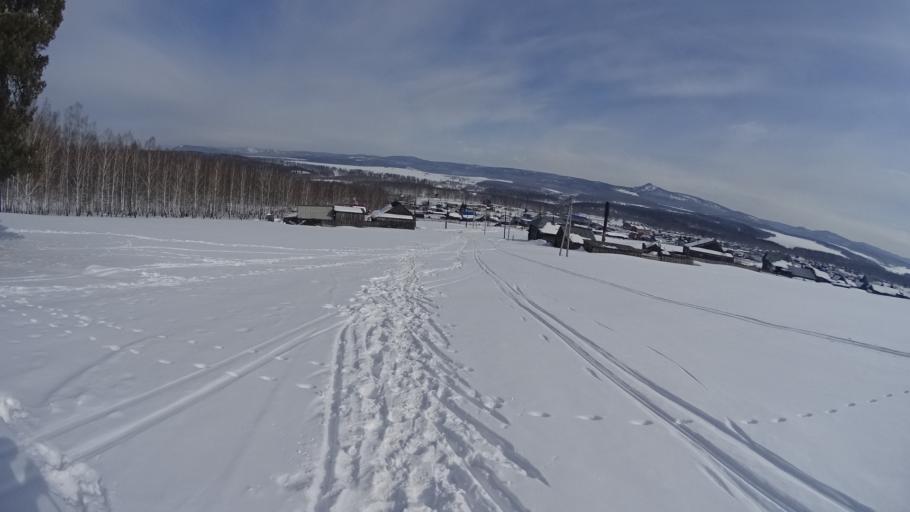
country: RU
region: Bashkortostan
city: Lomovka
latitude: 53.8080
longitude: 58.1963
